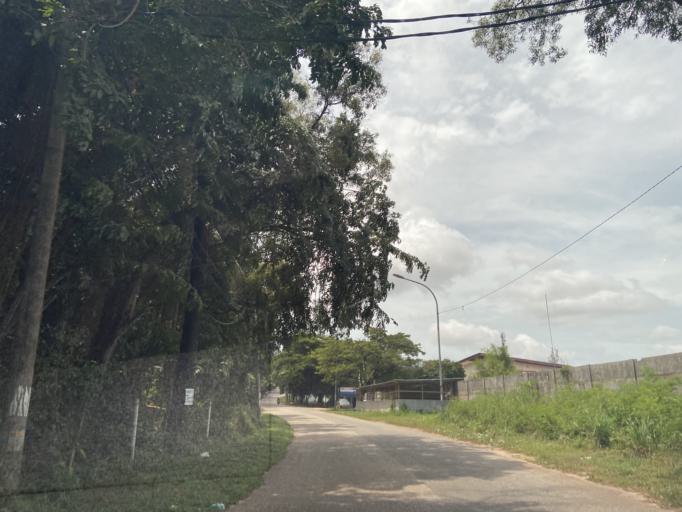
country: SG
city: Singapore
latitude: 1.1594
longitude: 104.0057
